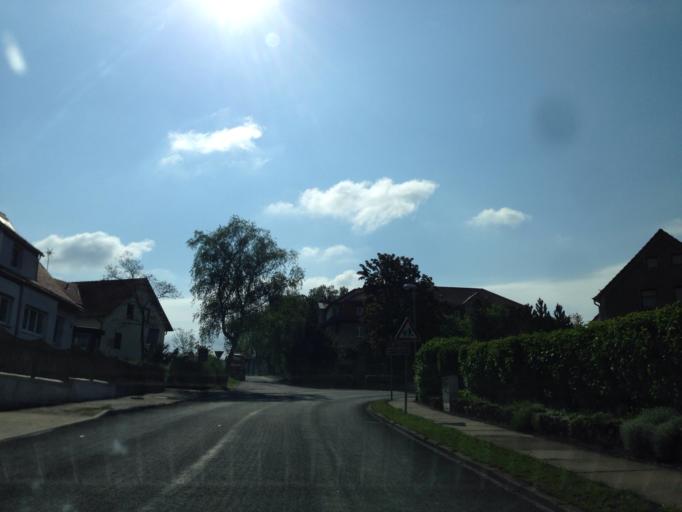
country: DE
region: Thuringia
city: Ranis
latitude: 50.6608
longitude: 11.5715
